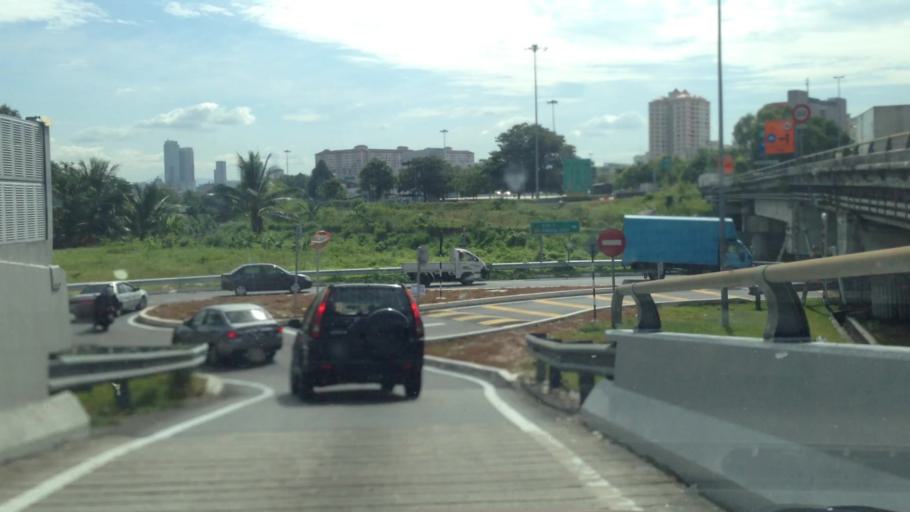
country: MY
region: Selangor
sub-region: Petaling
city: Petaling Jaya
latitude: 3.0769
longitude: 101.6209
